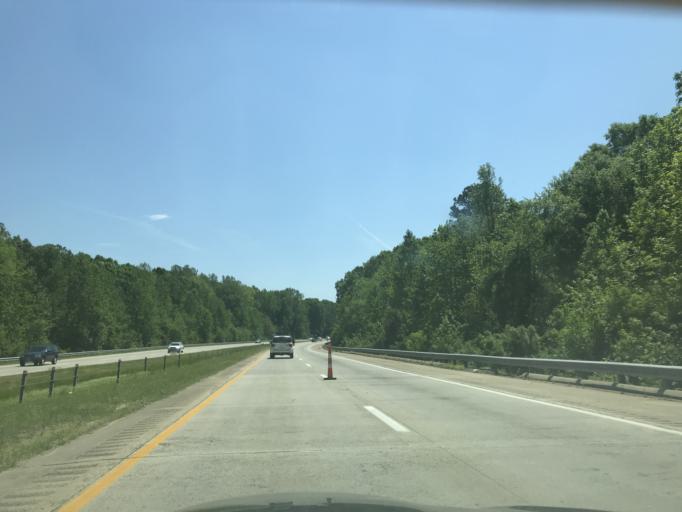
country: US
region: North Carolina
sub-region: Johnston County
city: Clayton
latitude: 35.5616
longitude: -78.5760
